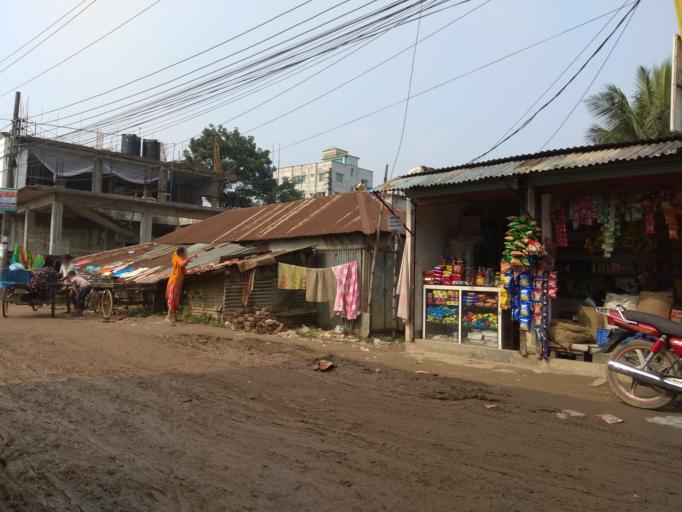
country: BD
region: Dhaka
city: Tungi
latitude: 23.8543
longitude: 90.3846
